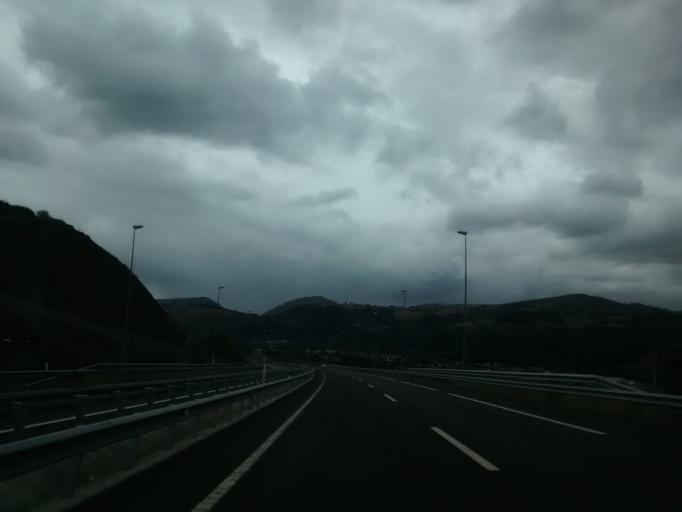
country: ES
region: Cantabria
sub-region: Provincia de Cantabria
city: Arenas de Iguna
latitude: 43.1659
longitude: -4.0525
